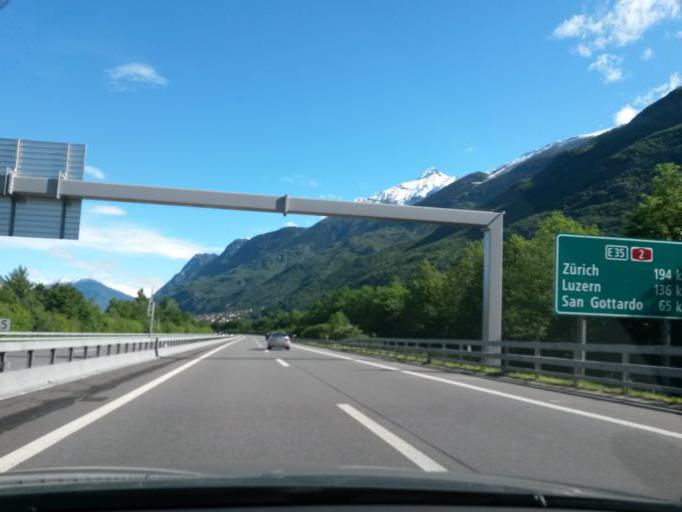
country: CH
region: Ticino
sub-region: Bellinzona District
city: Lumino
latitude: 46.2256
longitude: 9.0343
